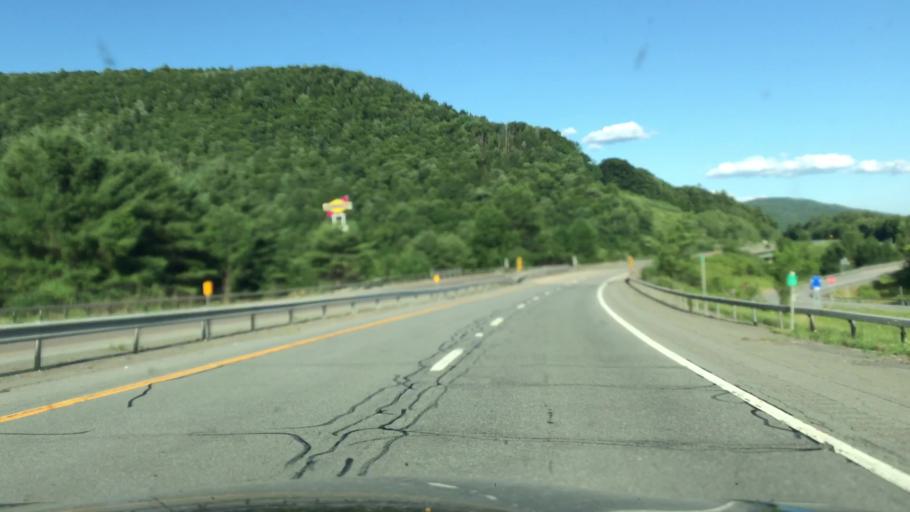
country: US
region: New York
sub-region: Delaware County
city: Hancock
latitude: 41.9927
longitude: -75.1333
